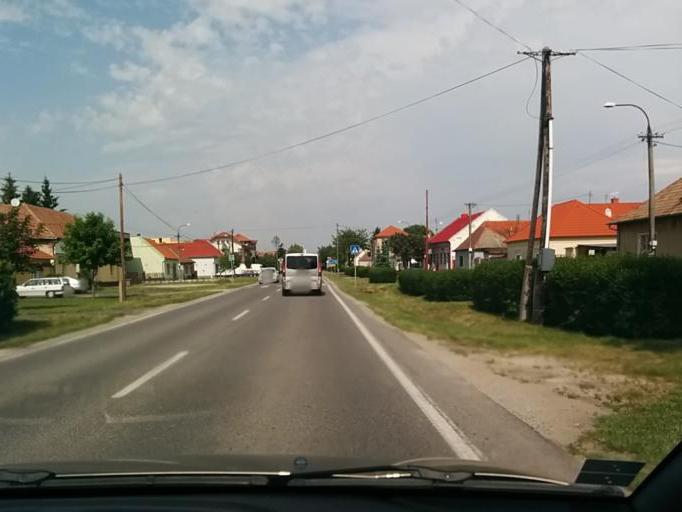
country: SK
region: Trnavsky
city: Sladkovicovo
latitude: 48.2013
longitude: 17.6364
